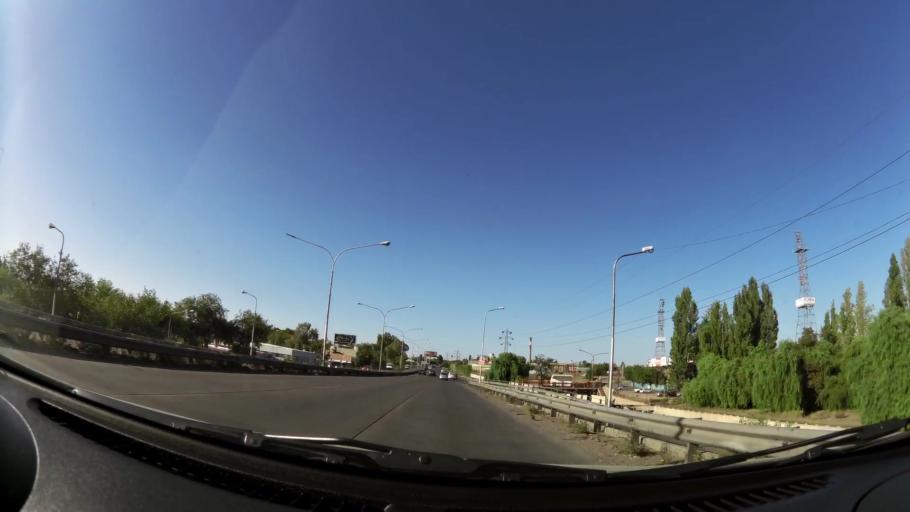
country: AR
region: Mendoza
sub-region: Departamento de Godoy Cruz
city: Godoy Cruz
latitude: -32.9194
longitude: -68.8376
